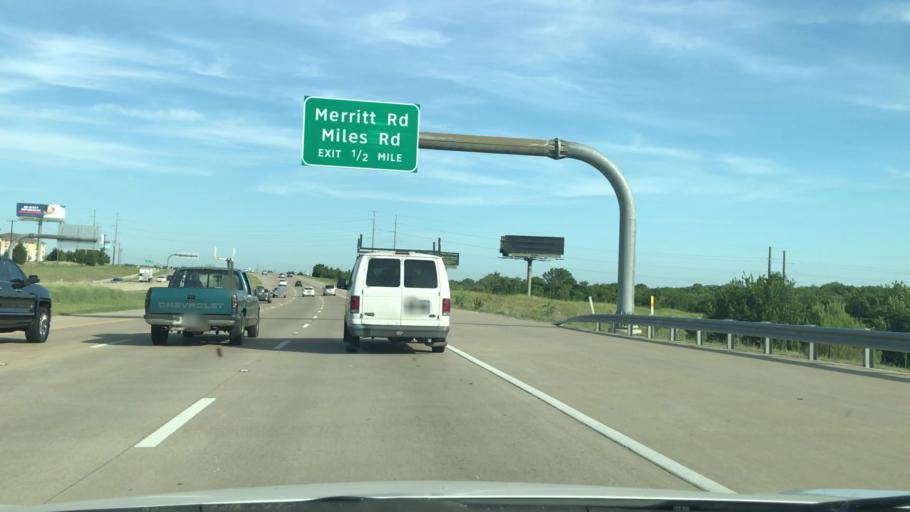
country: US
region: Texas
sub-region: Dallas County
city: Rowlett
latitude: 32.9456
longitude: -96.5596
